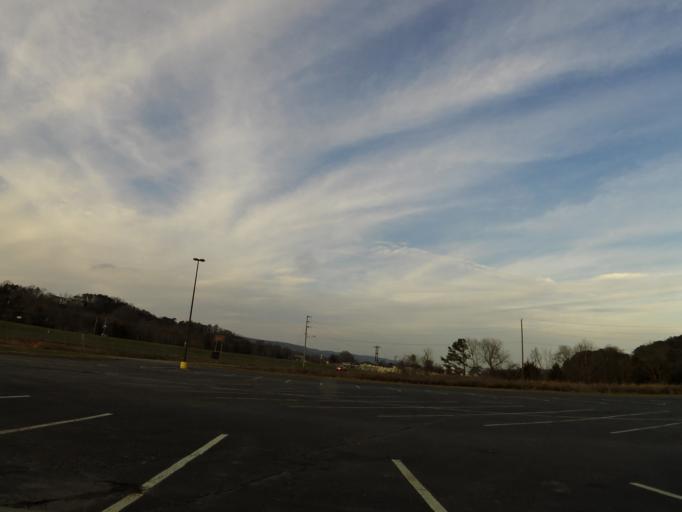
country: US
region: Tennessee
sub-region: Rhea County
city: Dayton
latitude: 35.4768
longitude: -85.0268
